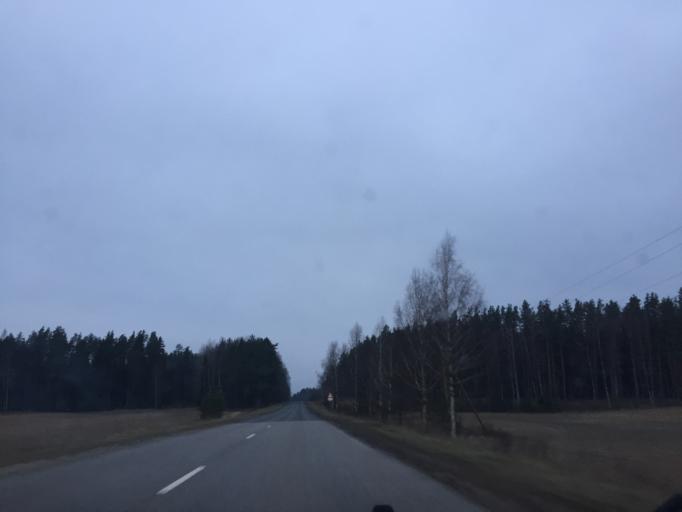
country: LV
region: Priekuli
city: Priekuli
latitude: 57.3247
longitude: 25.4333
